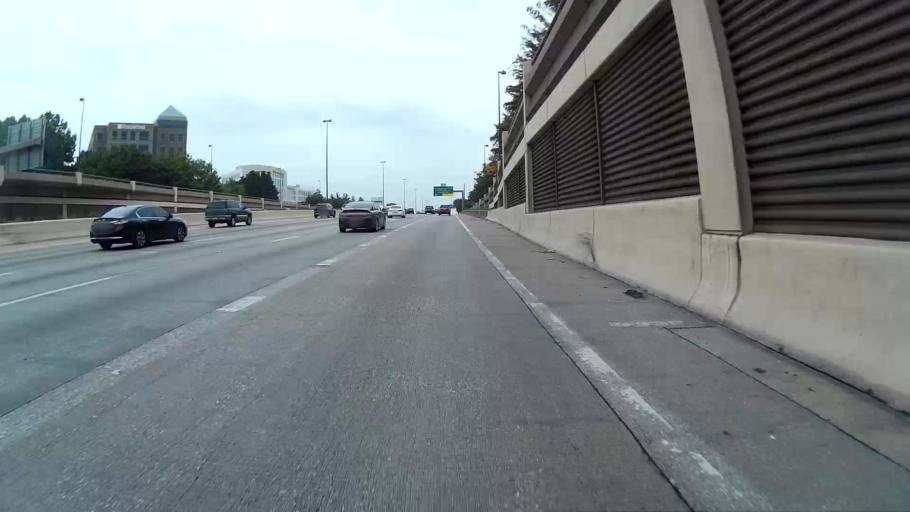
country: US
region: Texas
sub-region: Dallas County
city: University Park
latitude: 32.8724
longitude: -96.7700
